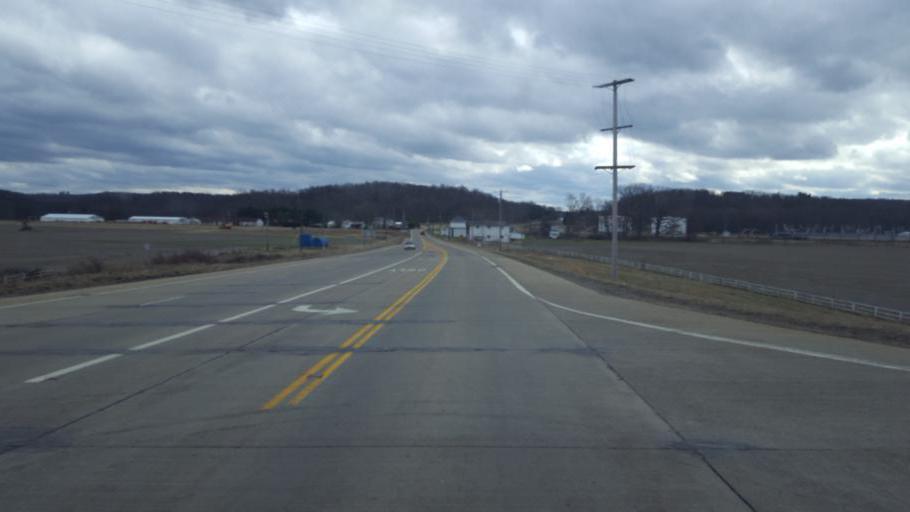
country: US
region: Ohio
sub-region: Muskingum County
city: Frazeysburg
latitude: 40.1026
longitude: -82.1742
